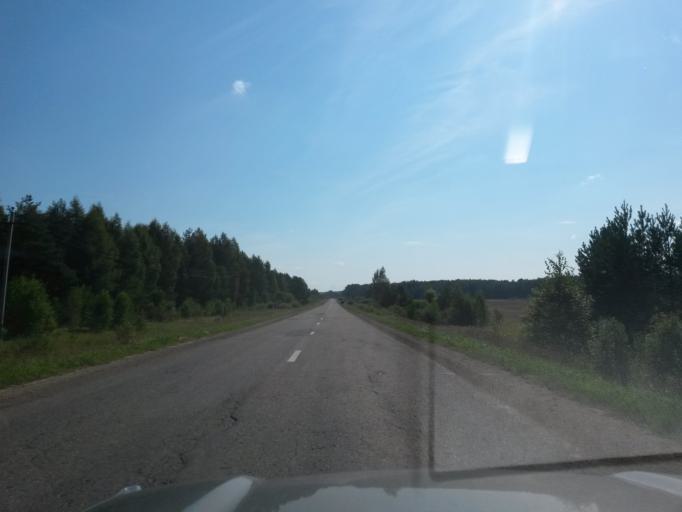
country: RU
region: Jaroslavl
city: Gavrilov-Yam
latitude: 57.3078
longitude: 39.9683
